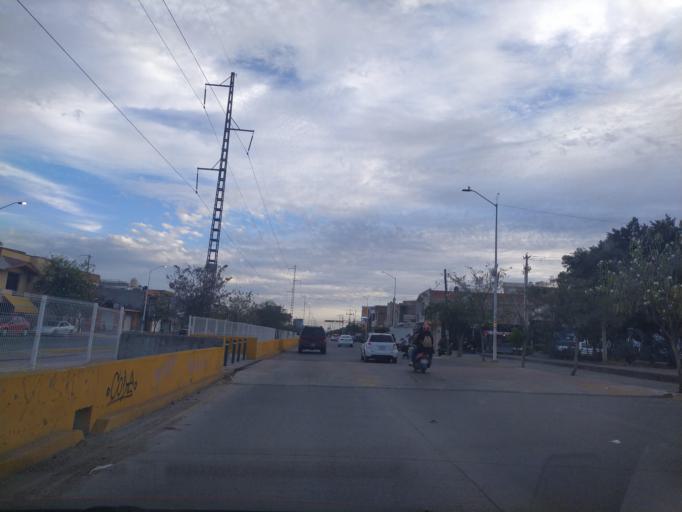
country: LA
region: Oudomxai
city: Muang La
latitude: 21.0259
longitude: 101.8695
